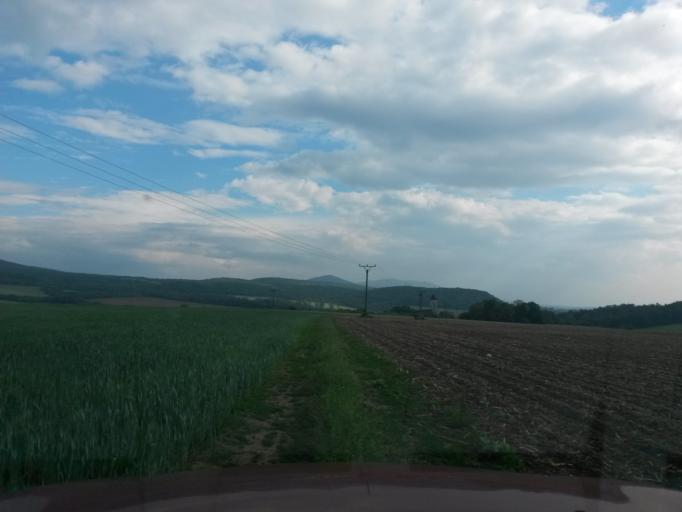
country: SK
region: Kosicky
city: Secovce
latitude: 48.7419
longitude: 21.4611
